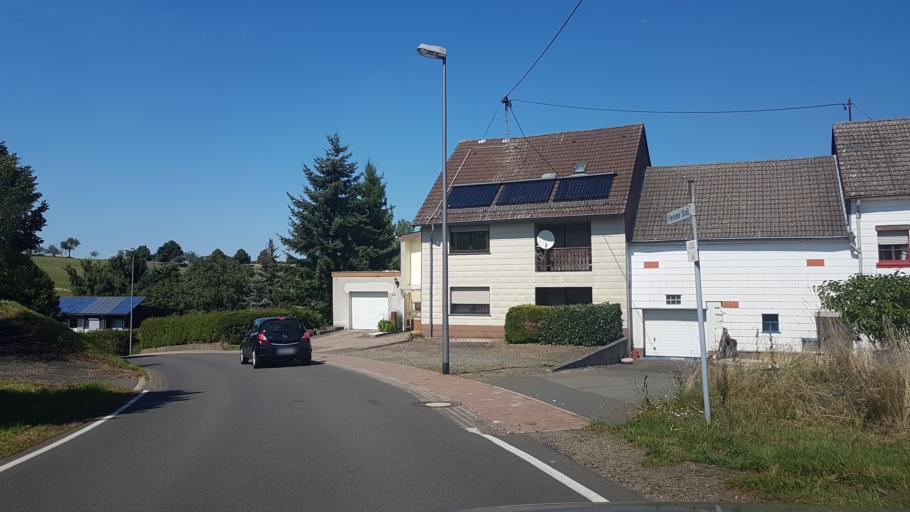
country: DE
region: Rheinland-Pfalz
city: Ruckweiler
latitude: 49.5771
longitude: 7.2373
